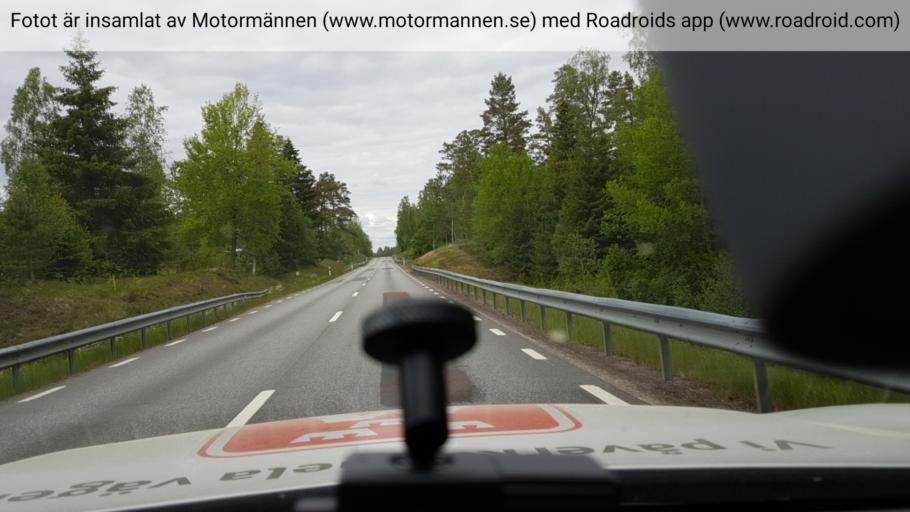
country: SE
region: Joenkoeping
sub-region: Mullsjo Kommun
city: Mullsjoe
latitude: 57.8605
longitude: 13.8579
